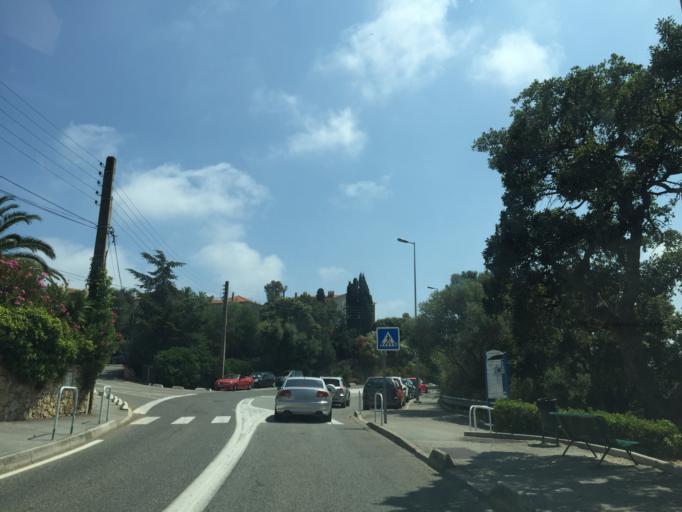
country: FR
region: Provence-Alpes-Cote d'Azur
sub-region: Departement du Var
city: Saint-Raphael
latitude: 43.4288
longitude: 6.8714
